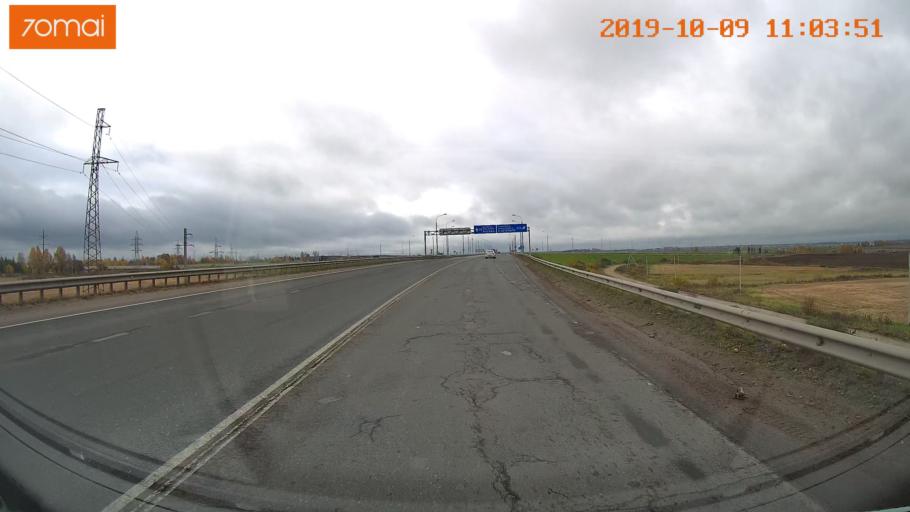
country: RU
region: Vologda
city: Vologda
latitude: 59.2181
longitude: 39.7735
